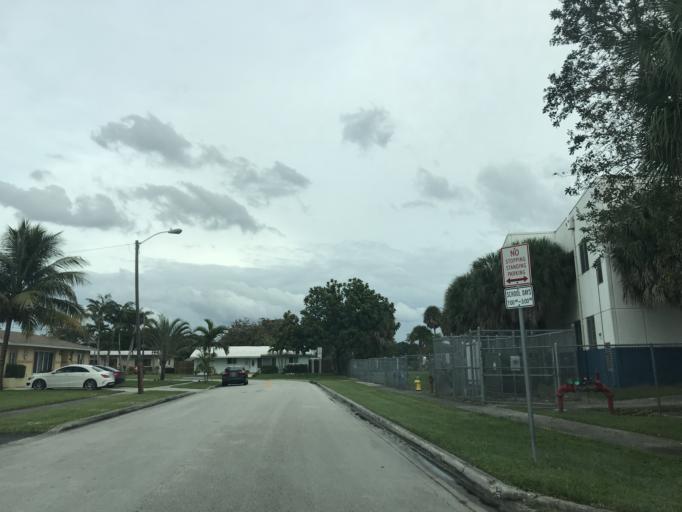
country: US
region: Florida
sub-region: Broward County
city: Margate
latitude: 26.2519
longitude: -80.2095
